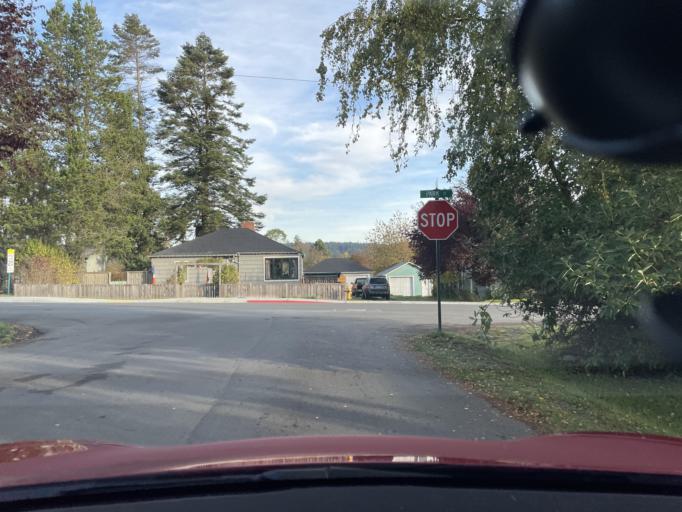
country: US
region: Washington
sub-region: San Juan County
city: Friday Harbor
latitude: 48.5343
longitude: -123.0243
